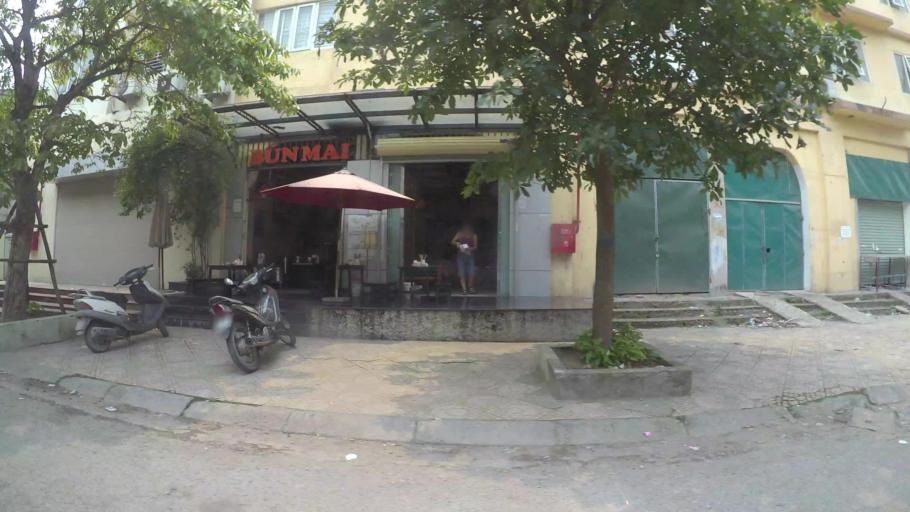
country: VN
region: Ha Noi
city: Ha Dong
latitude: 20.9737
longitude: 105.7642
